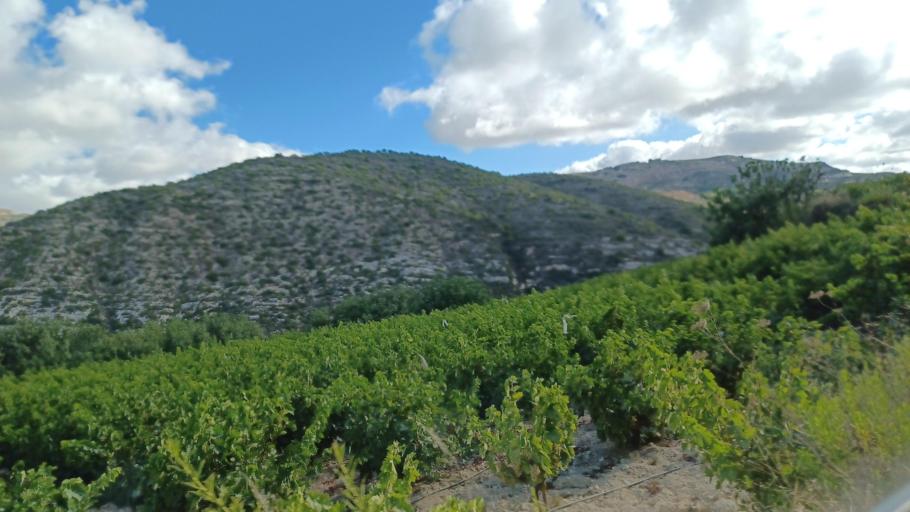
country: CY
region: Pafos
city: Tala
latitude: 34.8715
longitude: 32.4459
